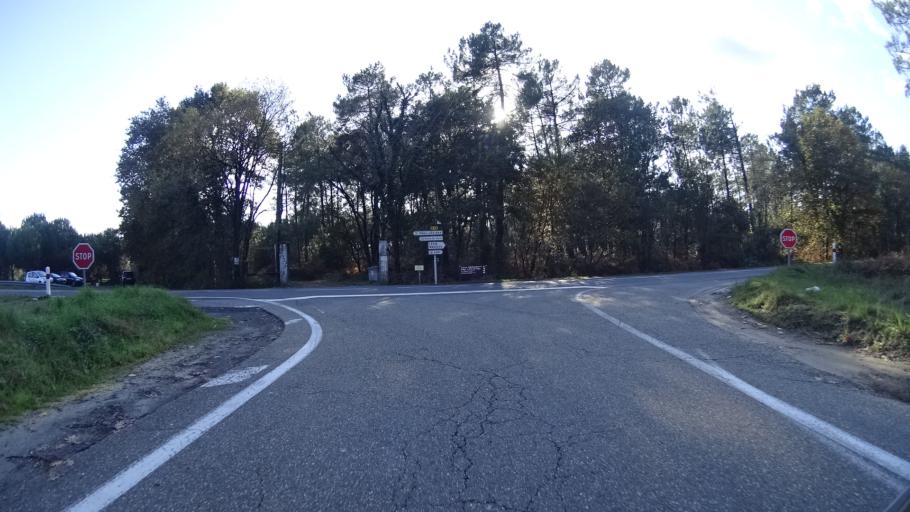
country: FR
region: Aquitaine
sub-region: Departement des Landes
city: Mees
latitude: 43.7329
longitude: -1.1031
